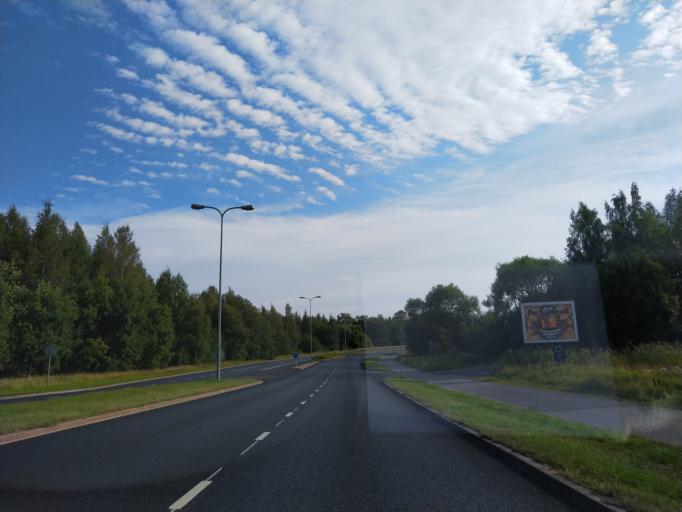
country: FI
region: Varsinais-Suomi
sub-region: Turku
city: Turku
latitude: 60.4257
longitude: 22.2395
